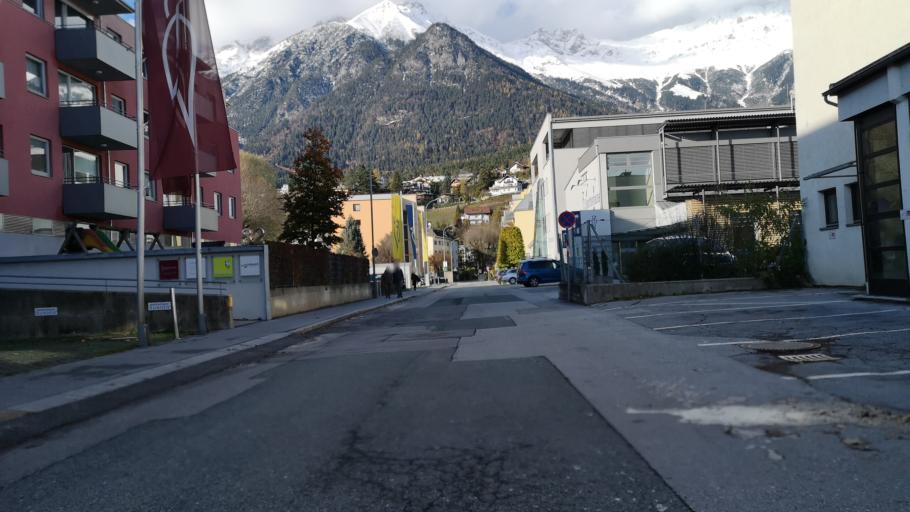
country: AT
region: Tyrol
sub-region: Innsbruck Stadt
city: Innsbruck
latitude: 47.2625
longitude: 11.3717
